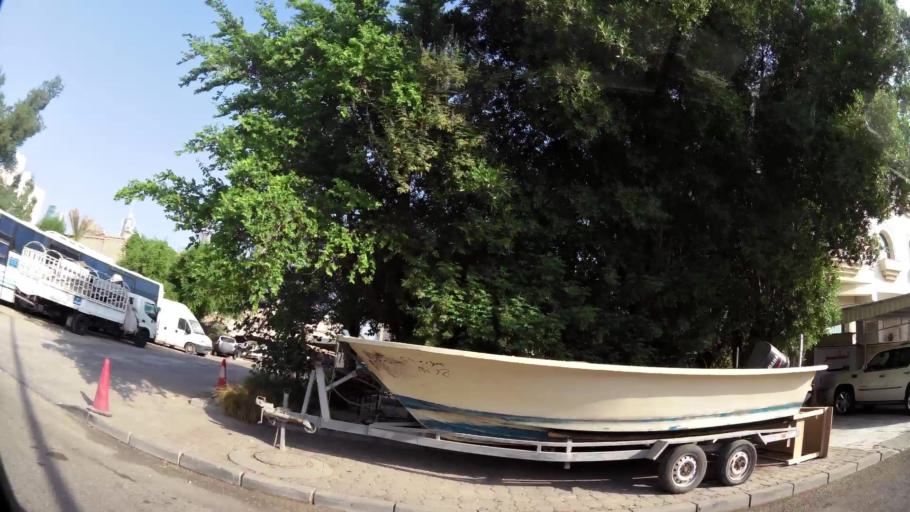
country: KW
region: Al Asimah
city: Ad Dasmah
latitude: 29.3687
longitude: 47.9987
